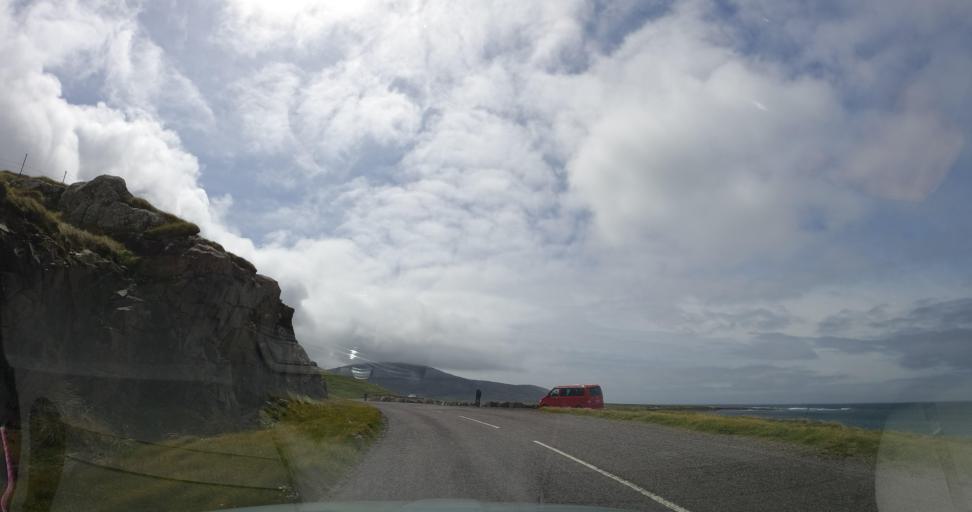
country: GB
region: Scotland
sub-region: Eilean Siar
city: Barra
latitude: 56.9916
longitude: -7.5085
